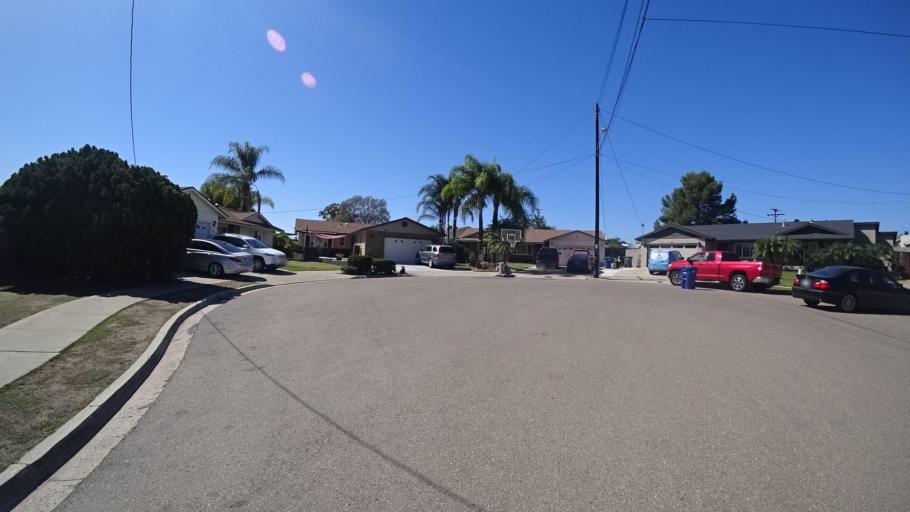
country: US
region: California
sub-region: San Diego County
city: La Presa
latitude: 32.6965
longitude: -117.0070
